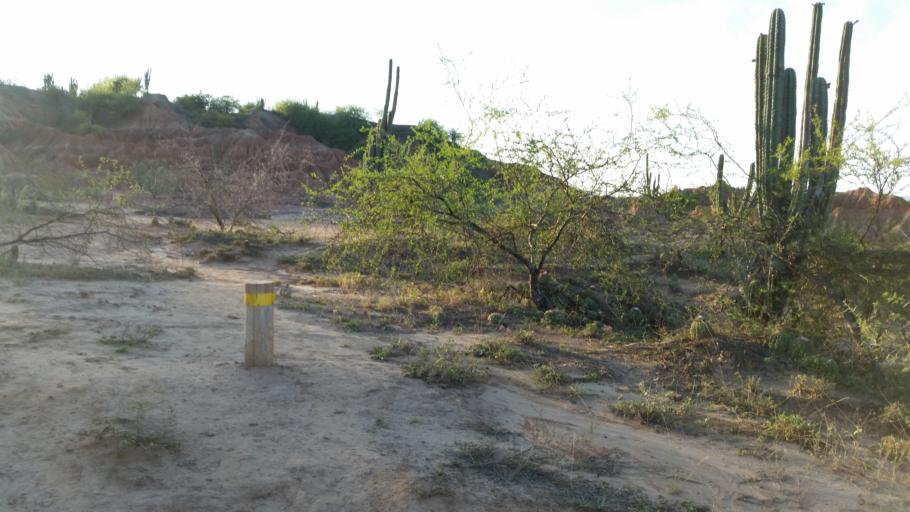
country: CO
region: Huila
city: Villavieja
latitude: 3.2298
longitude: -75.1719
